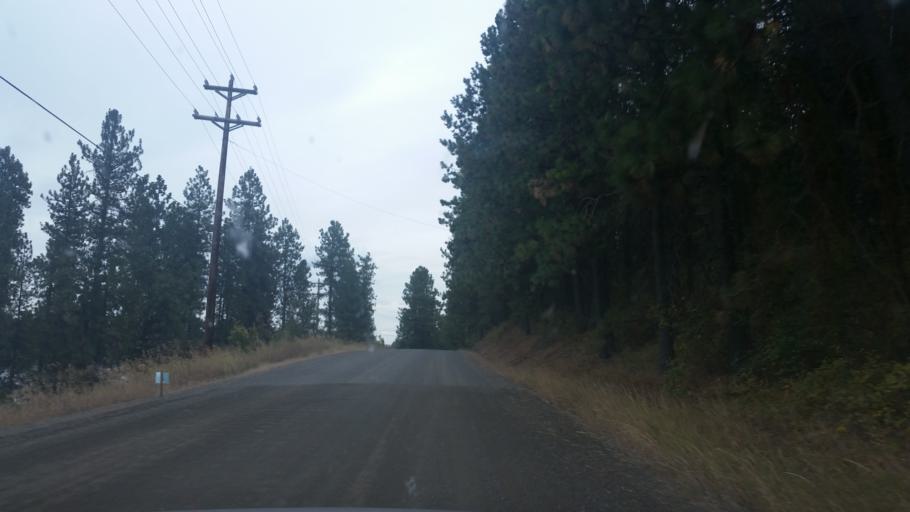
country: US
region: Washington
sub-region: Spokane County
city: Cheney
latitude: 47.5487
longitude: -117.5980
